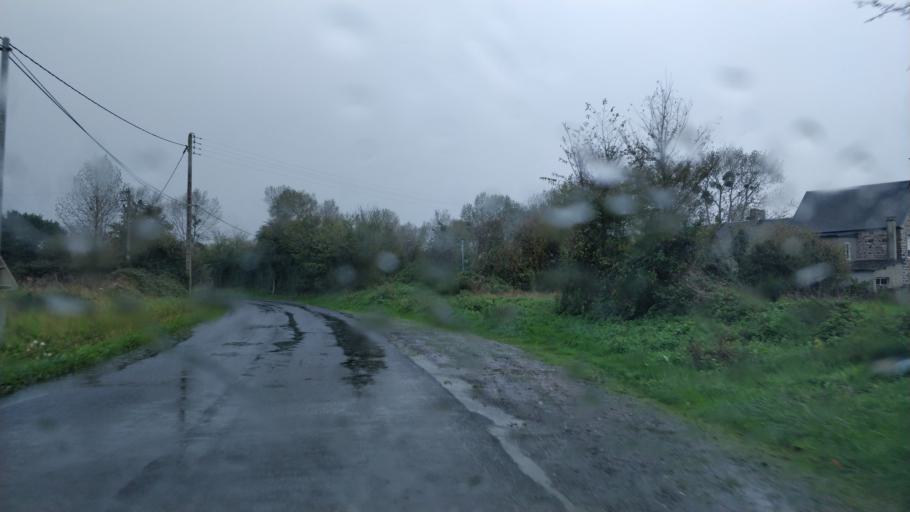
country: FR
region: Lower Normandy
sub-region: Departement de la Manche
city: Brehal
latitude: 48.9019
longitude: -1.5387
